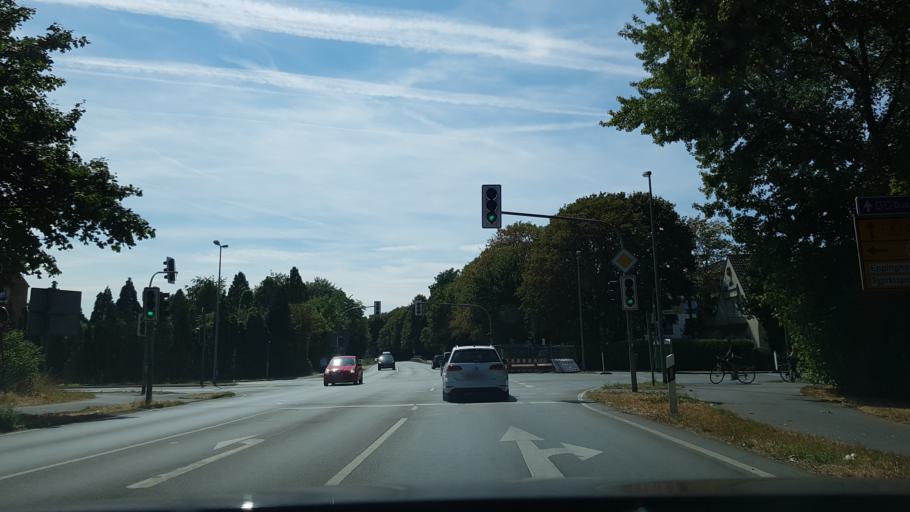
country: DE
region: North Rhine-Westphalia
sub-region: Regierungsbezirk Dusseldorf
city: Dinslaken
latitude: 51.5654
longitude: 6.7268
